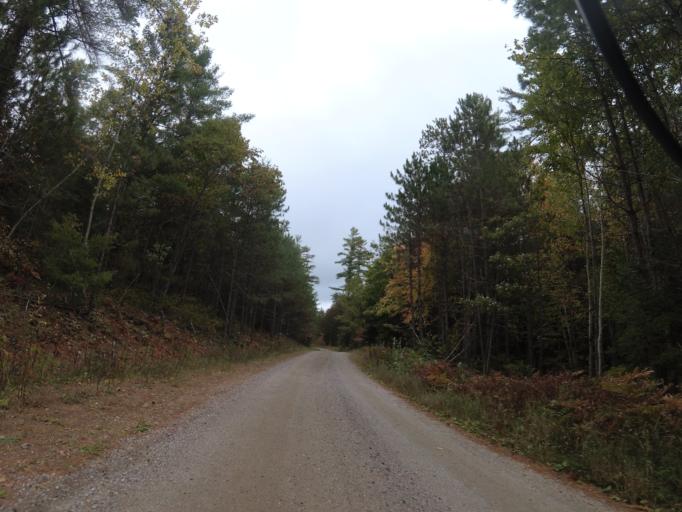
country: CA
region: Ontario
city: Renfrew
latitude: 45.2257
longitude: -77.0511
